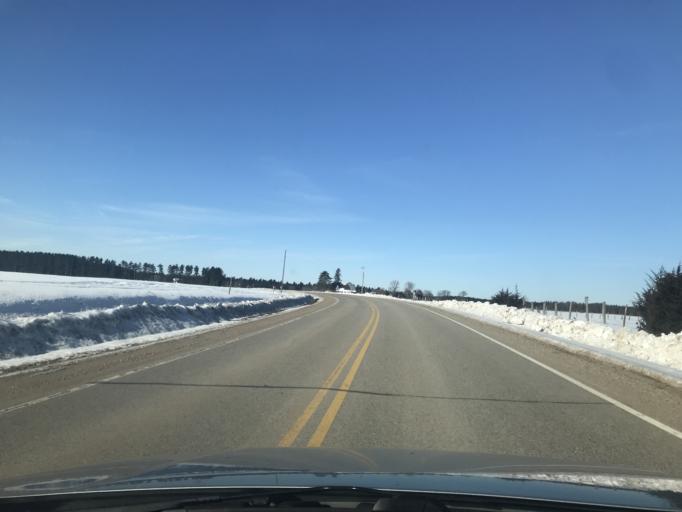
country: US
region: Wisconsin
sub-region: Marinette County
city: Niagara
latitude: 45.4288
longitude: -88.0255
